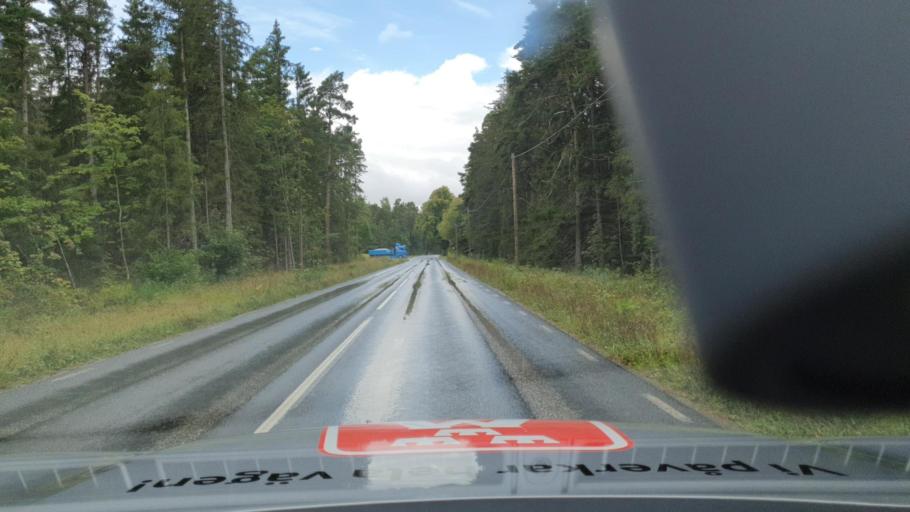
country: SE
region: Gotland
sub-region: Gotland
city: Visby
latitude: 57.5751
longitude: 18.5014
